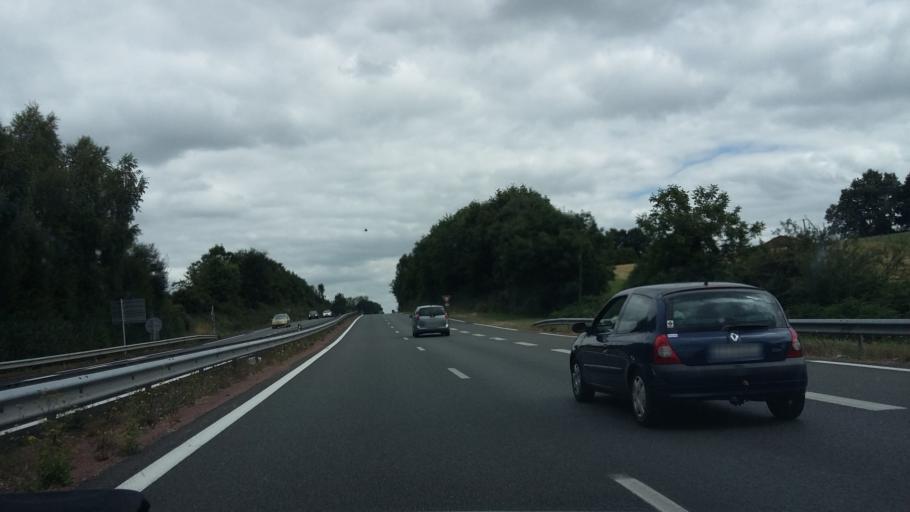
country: FR
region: Pays de la Loire
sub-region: Departement de la Vendee
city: Mouilleron-le-Captif
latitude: 46.6880
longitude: -1.4598
